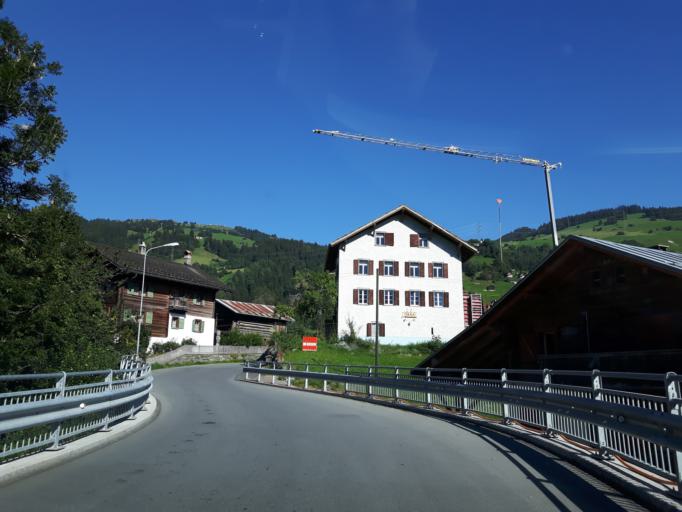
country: CH
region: Grisons
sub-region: Surselva District
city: Breil
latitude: 46.7745
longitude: 9.1097
